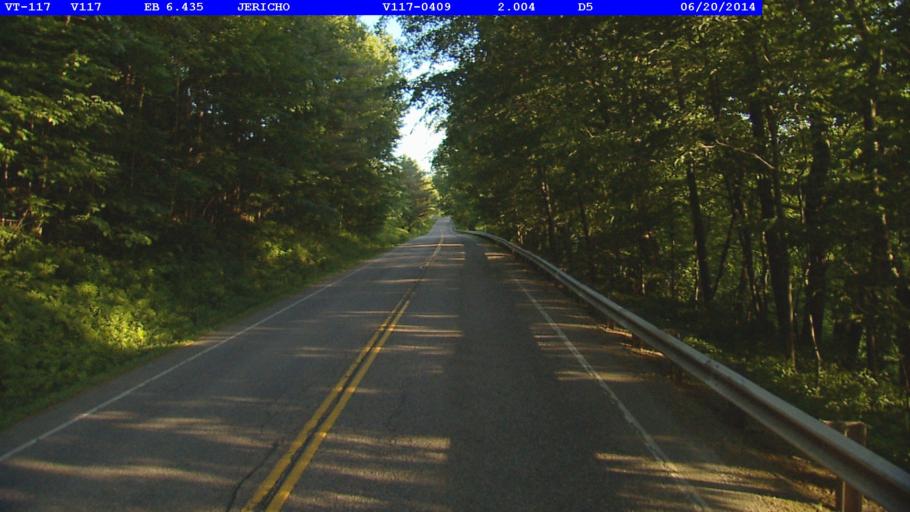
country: US
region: Vermont
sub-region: Chittenden County
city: Williston
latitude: 44.4465
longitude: -73.0189
